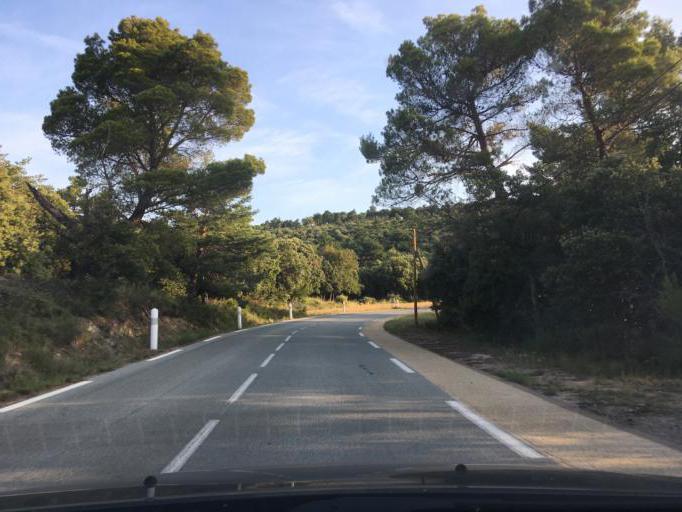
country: FR
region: Provence-Alpes-Cote d'Azur
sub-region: Departement du Var
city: Aups
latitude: 43.6594
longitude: 6.2226
